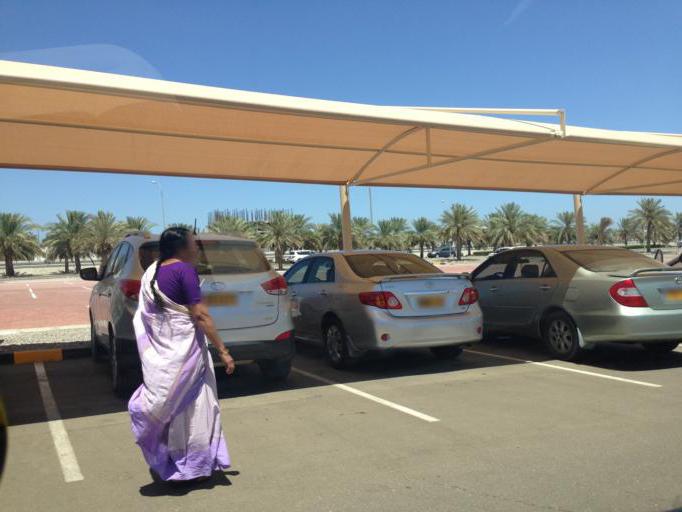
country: OM
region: Muhafazat Masqat
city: As Sib al Jadidah
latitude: 23.6490
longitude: 58.2149
